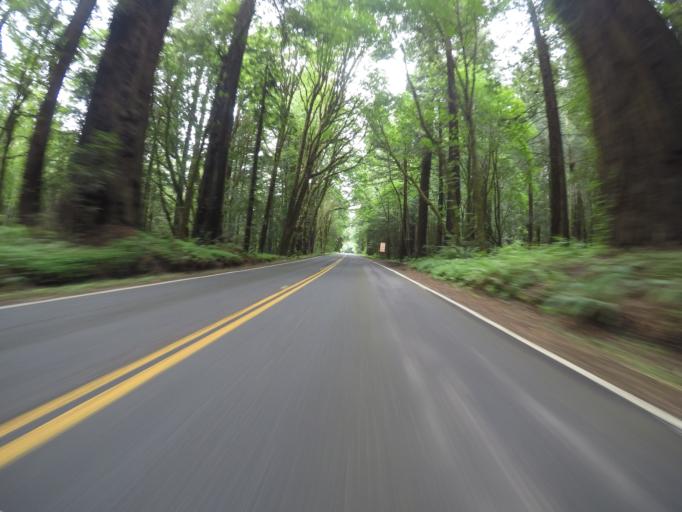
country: US
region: California
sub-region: Humboldt County
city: Rio Dell
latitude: 40.4417
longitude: -124.0297
